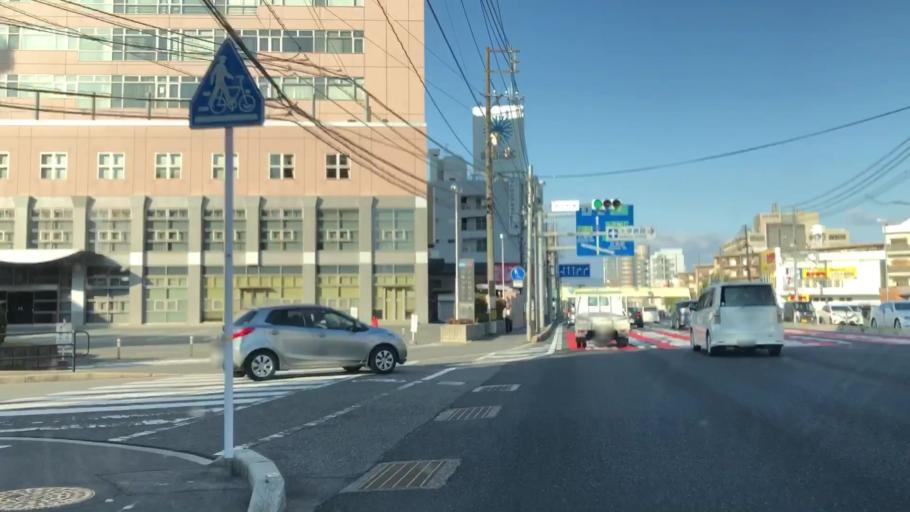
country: JP
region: Hiroshima
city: Hiroshima-shi
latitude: 34.3782
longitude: 132.4754
